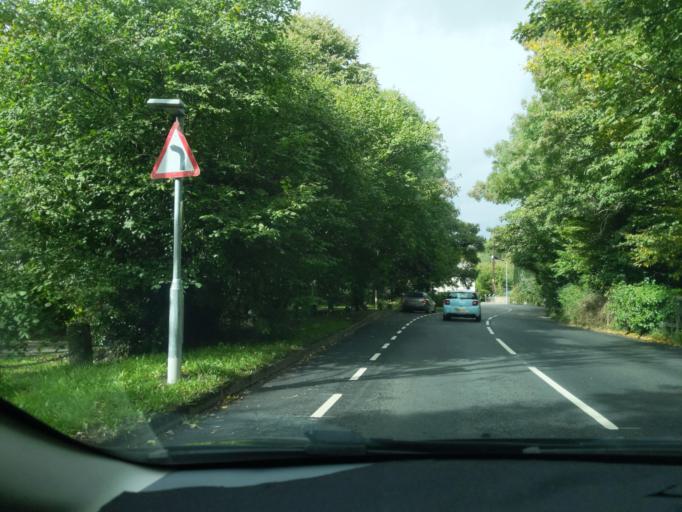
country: GB
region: England
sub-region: Cornwall
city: Par
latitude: 50.3582
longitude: -4.7052
